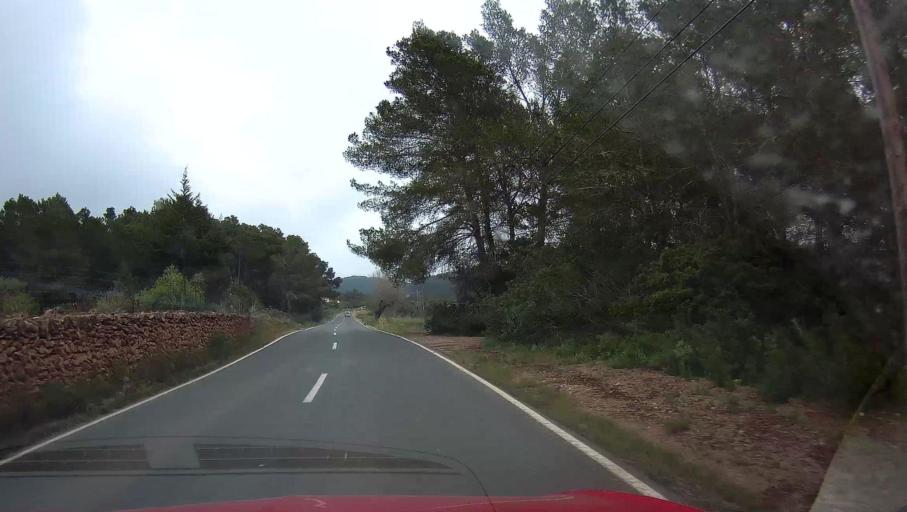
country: ES
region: Balearic Islands
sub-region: Illes Balears
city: Sant Joan de Labritja
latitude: 39.0681
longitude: 1.4893
